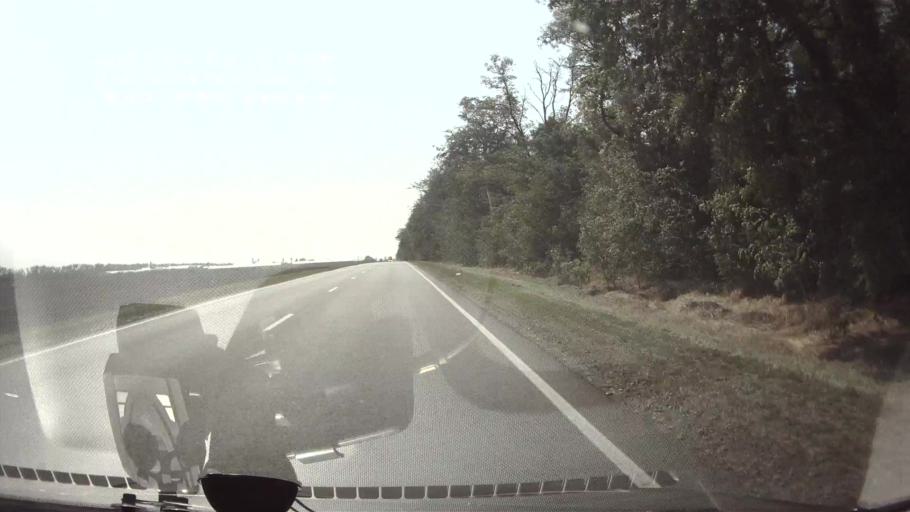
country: RU
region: Krasnodarskiy
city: Kavkazskaya
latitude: 45.4901
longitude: 40.6803
